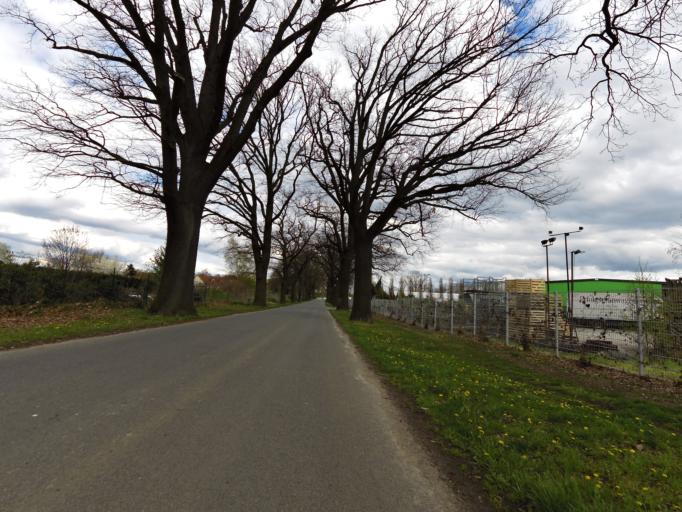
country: DE
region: Berlin
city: Lichtenrade
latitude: 52.3755
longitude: 13.4395
